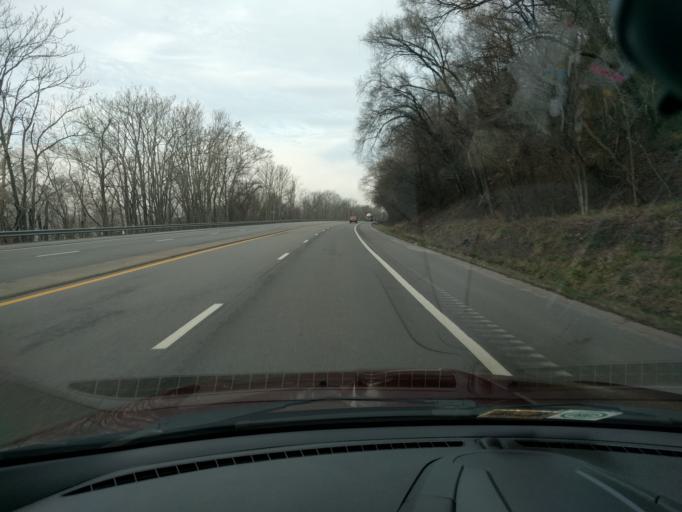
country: US
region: West Virginia
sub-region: Kanawha County
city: Marmet
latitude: 38.2498
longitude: -81.5609
